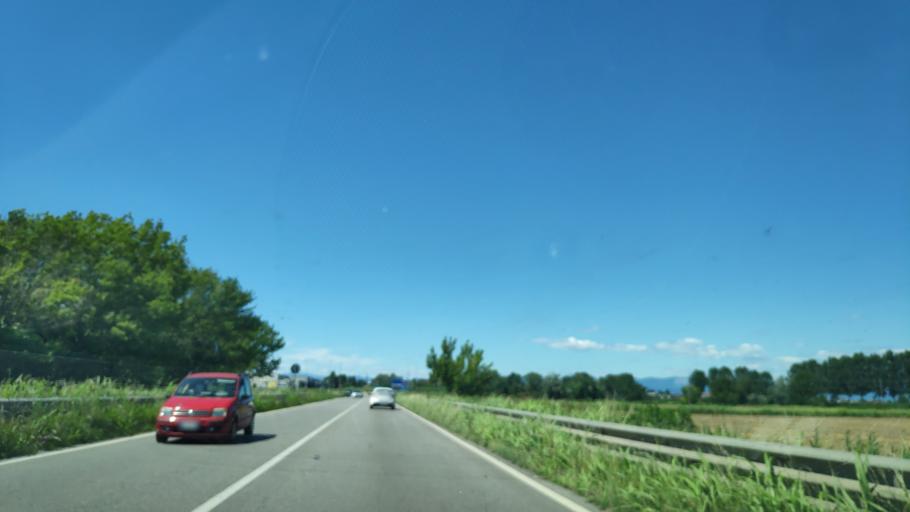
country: IT
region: Lombardy
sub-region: Citta metropolitana di Milano
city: Melzo
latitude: 45.4840
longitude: 9.4257
